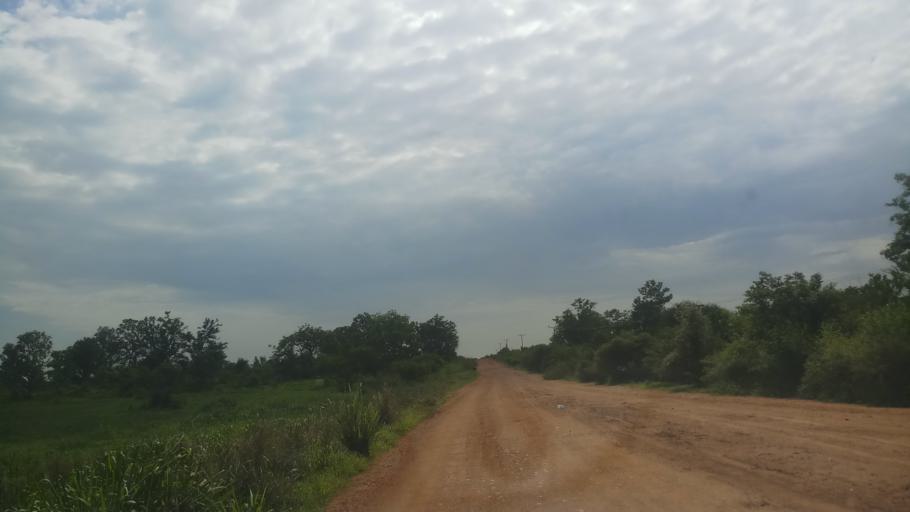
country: ET
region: Gambela
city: Gambela
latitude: 8.2142
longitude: 34.5551
